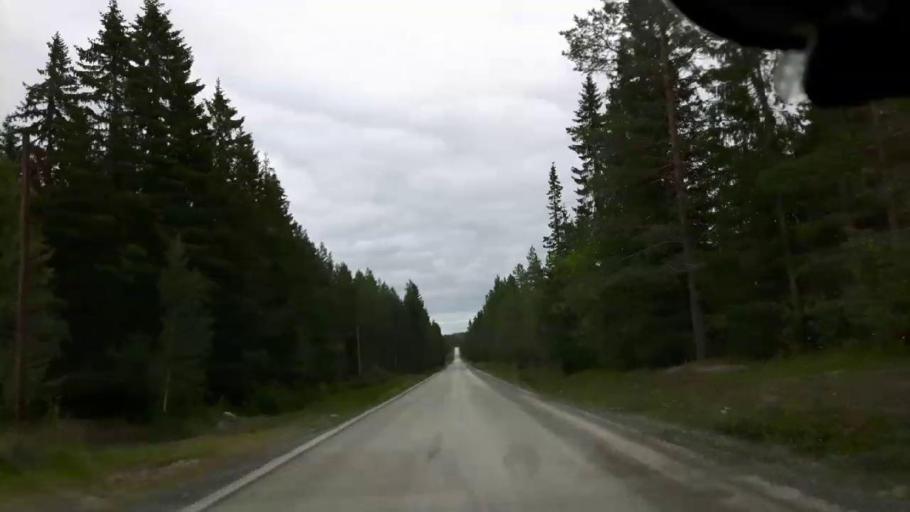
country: SE
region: Jaemtland
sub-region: OEstersunds Kommun
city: Brunflo
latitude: 63.1002
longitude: 15.1139
